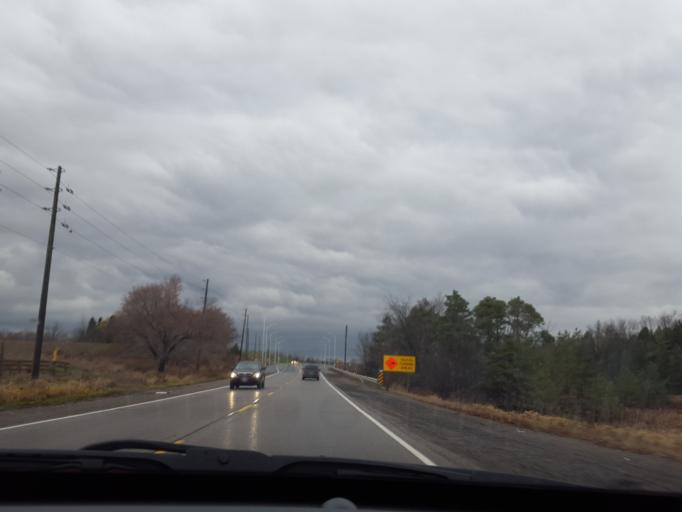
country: CA
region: Ontario
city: Pickering
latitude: 43.8986
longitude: -79.0956
